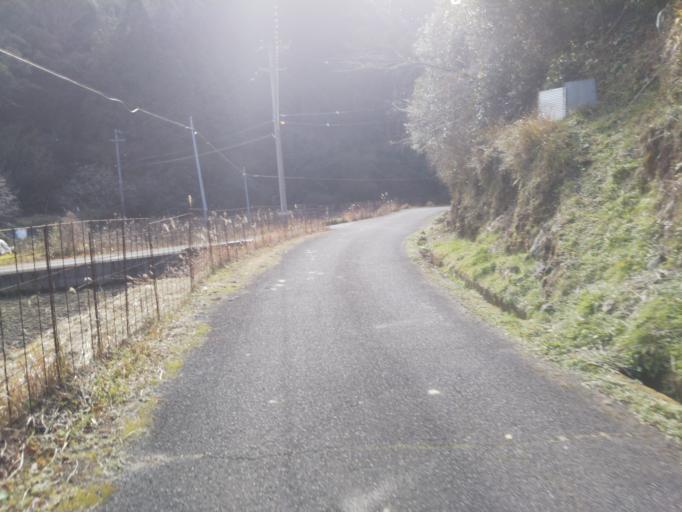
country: JP
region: Kochi
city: Nakamura
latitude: 33.0442
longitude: 132.9875
